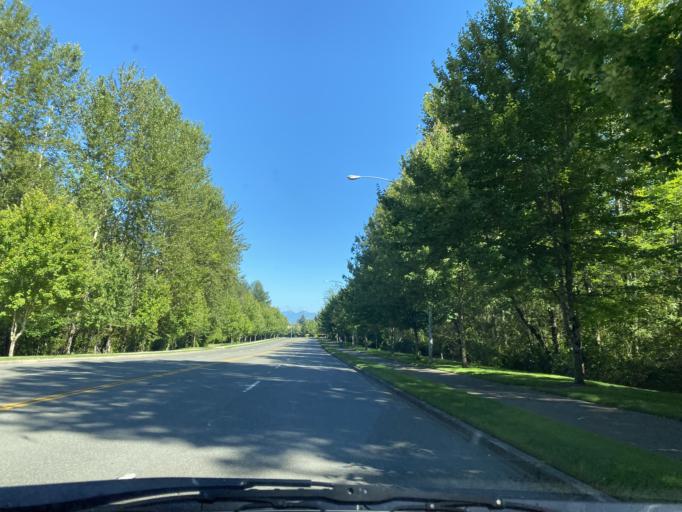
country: US
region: Washington
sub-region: Pierce County
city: South Hill
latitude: 47.1137
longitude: -122.2634
